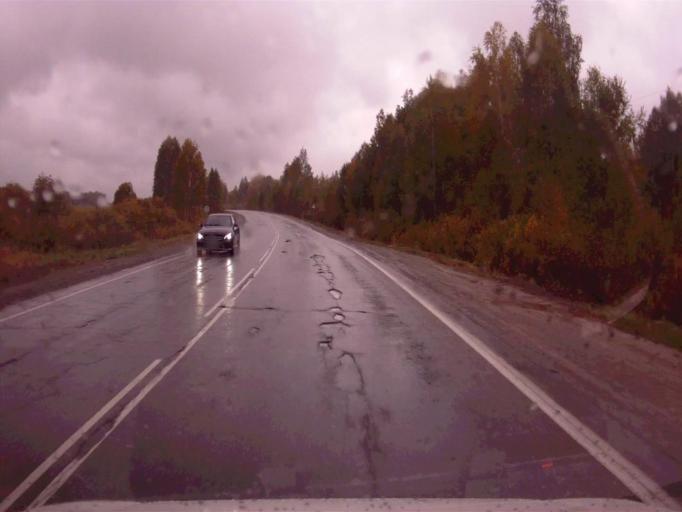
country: RU
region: Chelyabinsk
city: Argayash
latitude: 55.4861
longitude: 60.7373
